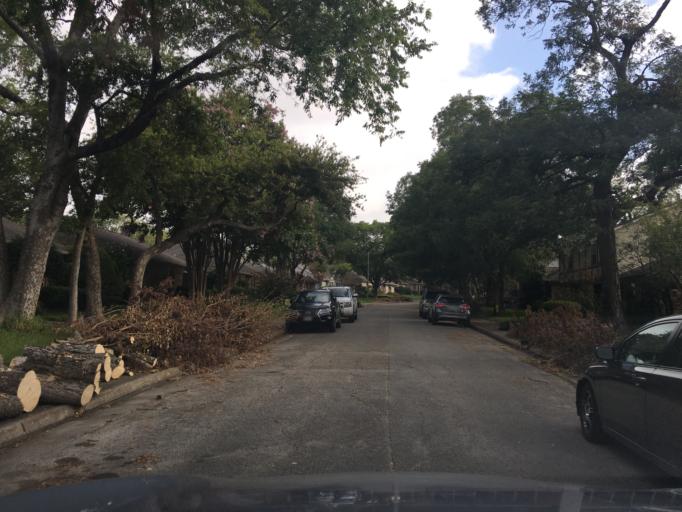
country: US
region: Texas
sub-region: Dallas County
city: Richardson
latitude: 32.8953
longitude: -96.7488
